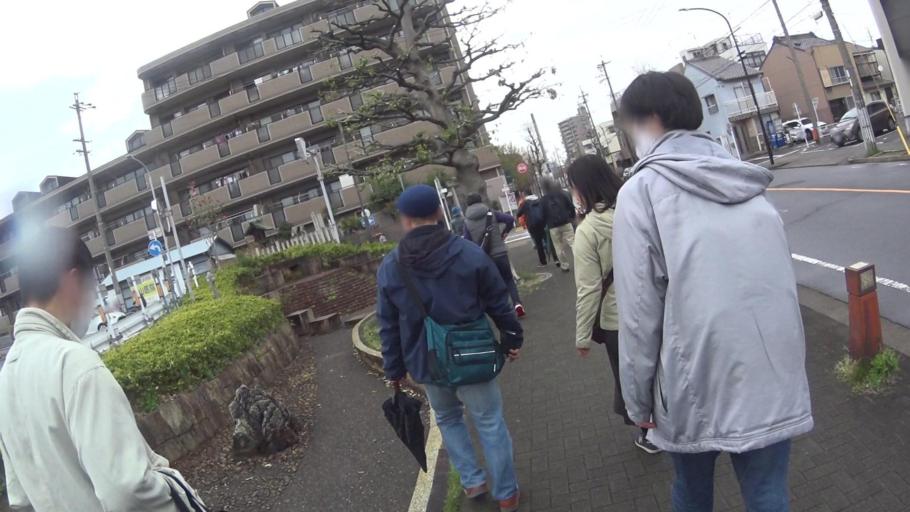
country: JP
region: Aichi
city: Nagoya-shi
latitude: 35.1201
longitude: 136.9040
